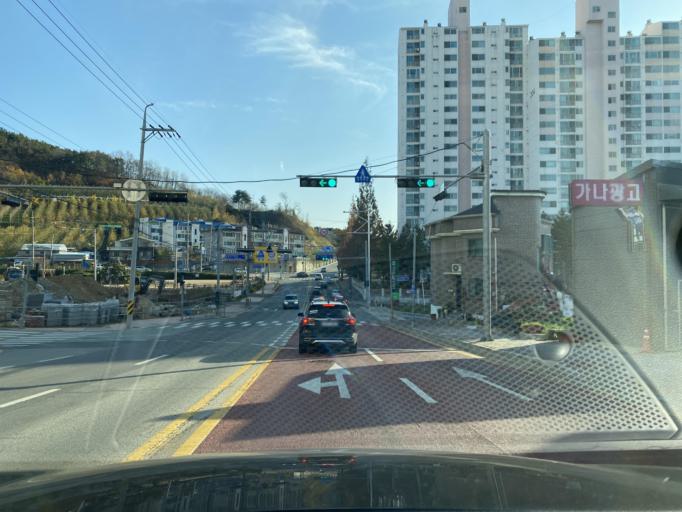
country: KR
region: Chungcheongnam-do
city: Yesan
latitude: 36.6879
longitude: 126.8359
